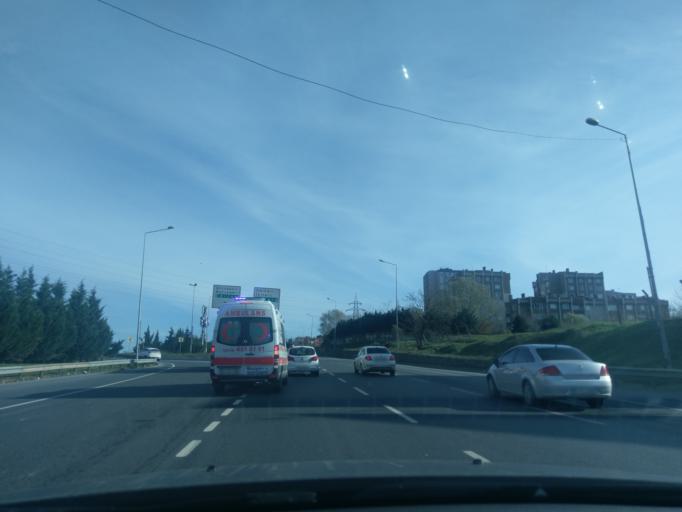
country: TR
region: Istanbul
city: Basaksehir
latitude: 41.0622
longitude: 28.7808
